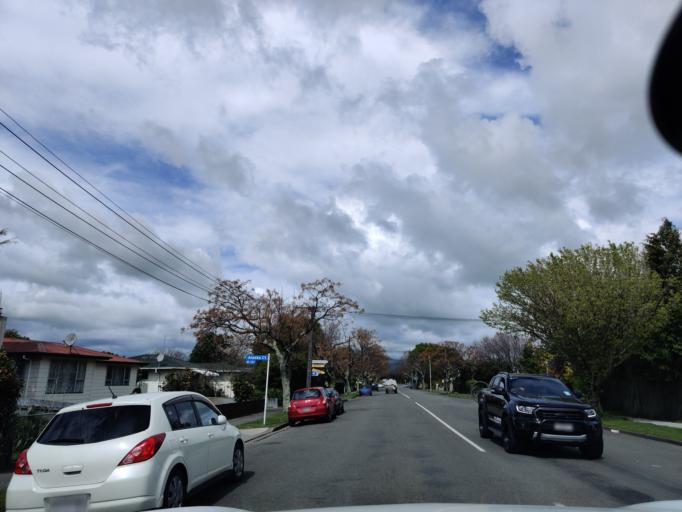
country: NZ
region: Manawatu-Wanganui
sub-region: Palmerston North City
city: Palmerston North
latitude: -40.3800
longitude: 175.5852
